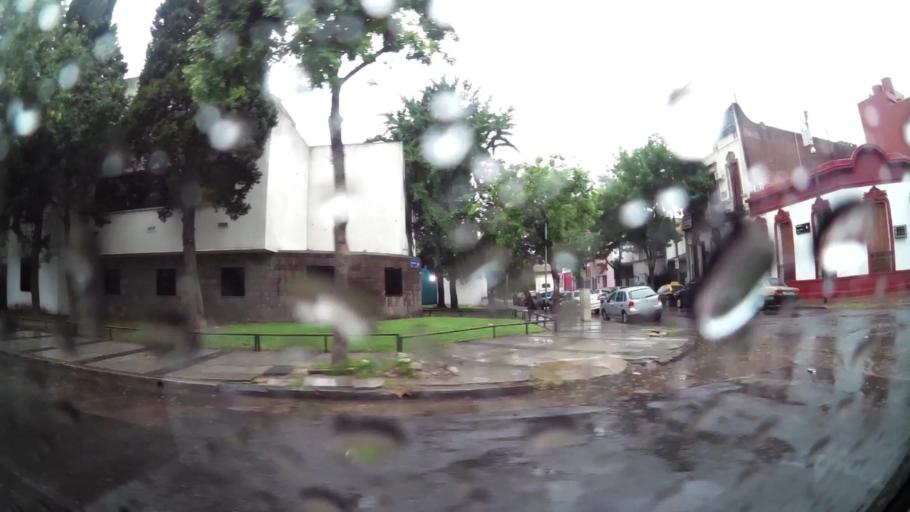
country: AR
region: Buenos Aires
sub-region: Partido de Avellaneda
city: Avellaneda
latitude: -34.6413
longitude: -58.3718
